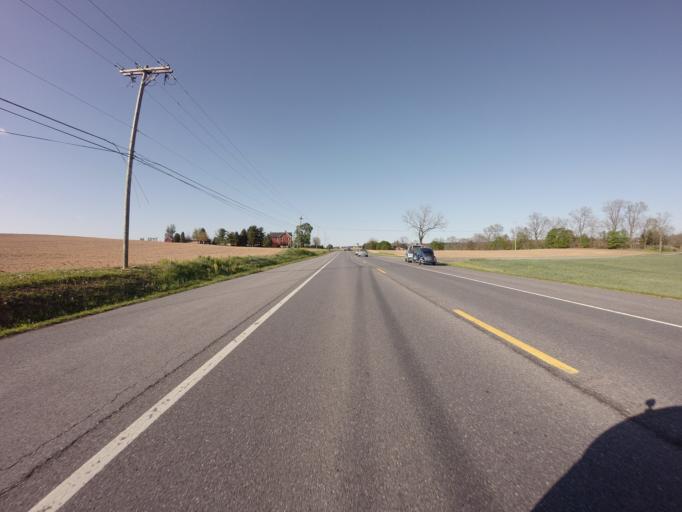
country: US
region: Maryland
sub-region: Frederick County
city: Walkersville
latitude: 39.4979
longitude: -77.3282
